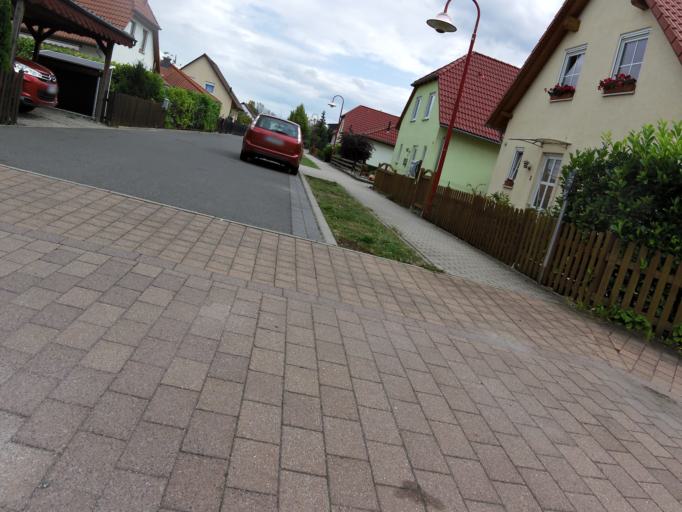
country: DE
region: Saxony
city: Rackwitz
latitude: 51.3881
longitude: 12.3715
